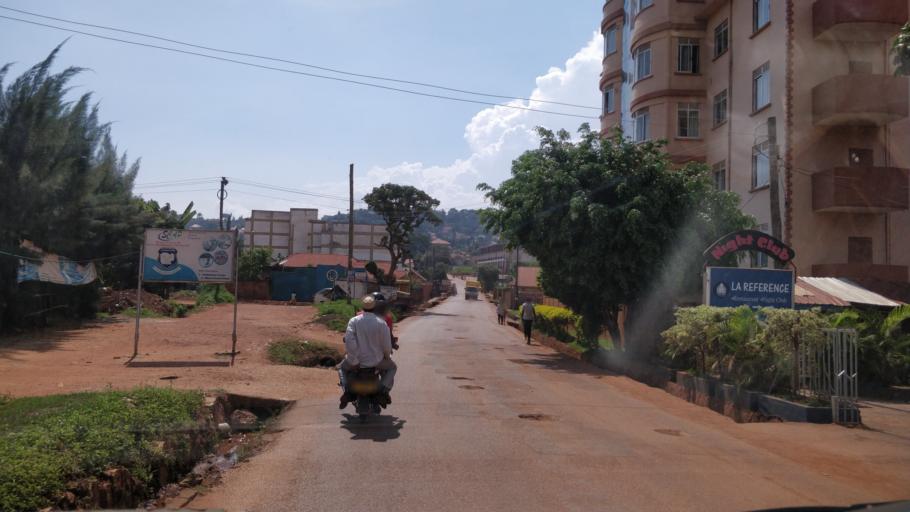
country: UG
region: Central Region
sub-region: Kampala District
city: Kampala
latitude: 0.2698
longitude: 32.6180
